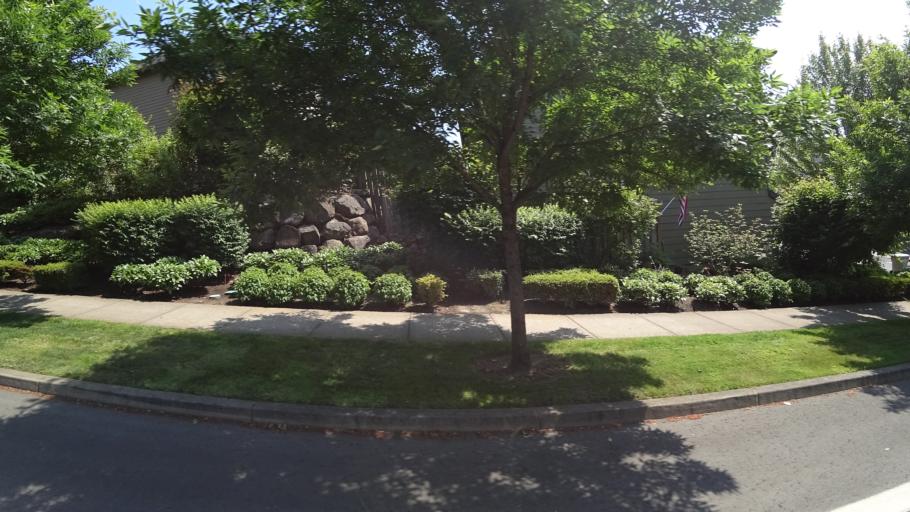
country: US
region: Oregon
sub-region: Clackamas County
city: Happy Valley
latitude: 45.4414
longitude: -122.5597
